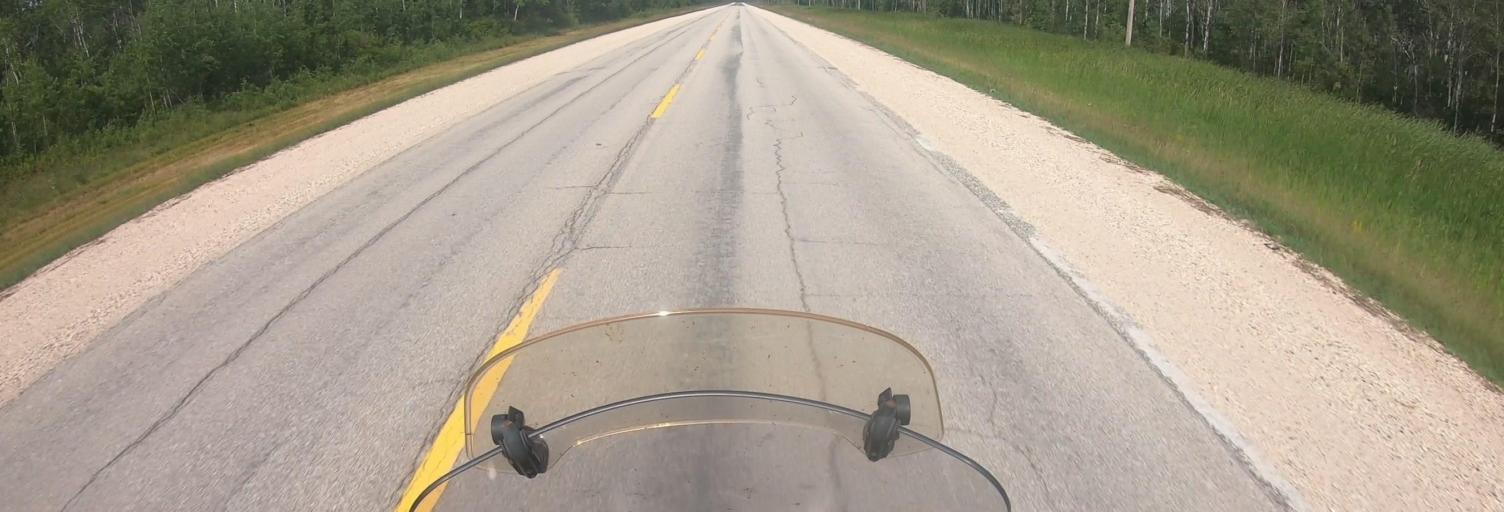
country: CA
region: Manitoba
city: Steinbach
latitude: 49.3498
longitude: -96.6493
